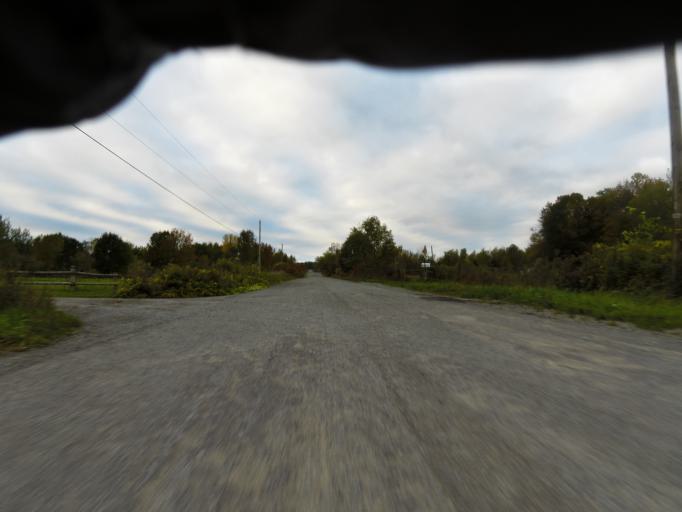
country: CA
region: Ontario
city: Quinte West
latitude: 44.0147
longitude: -77.8113
